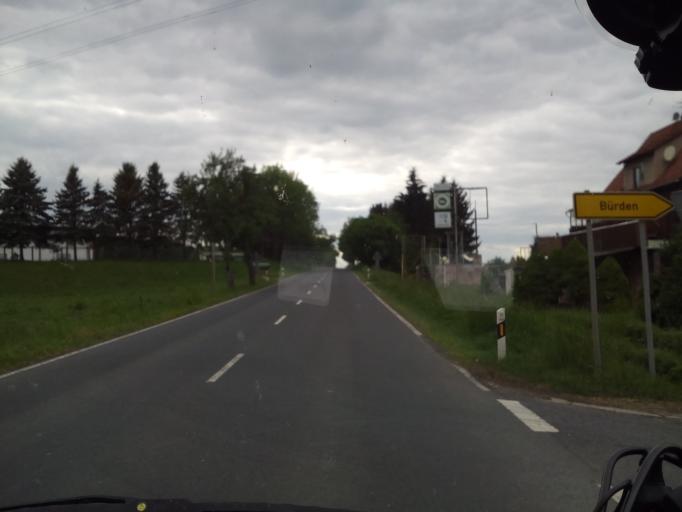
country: DE
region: Thuringia
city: Veilsdorf
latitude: 50.4153
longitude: 10.8064
